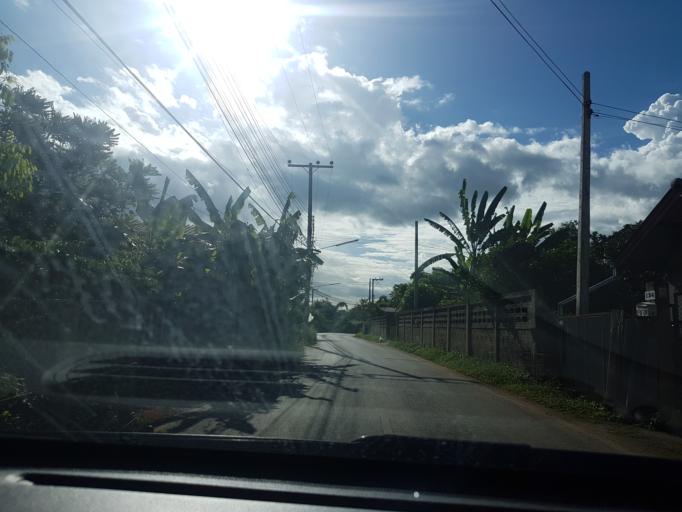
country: TH
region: Lampang
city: Ko Kha
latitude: 18.2328
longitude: 99.4269
